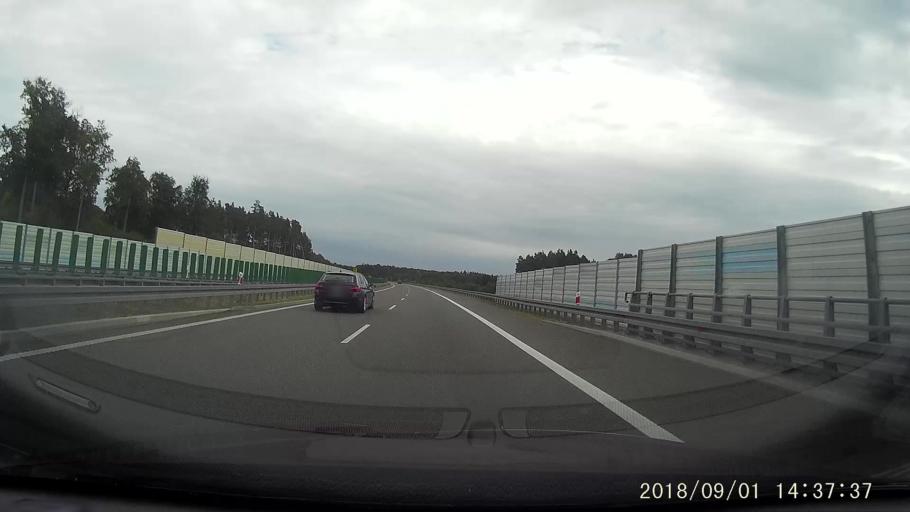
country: PL
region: West Pomeranian Voivodeship
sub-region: Powiat mysliborski
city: Nowogrodek Pomorski
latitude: 52.8437
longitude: 15.0453
